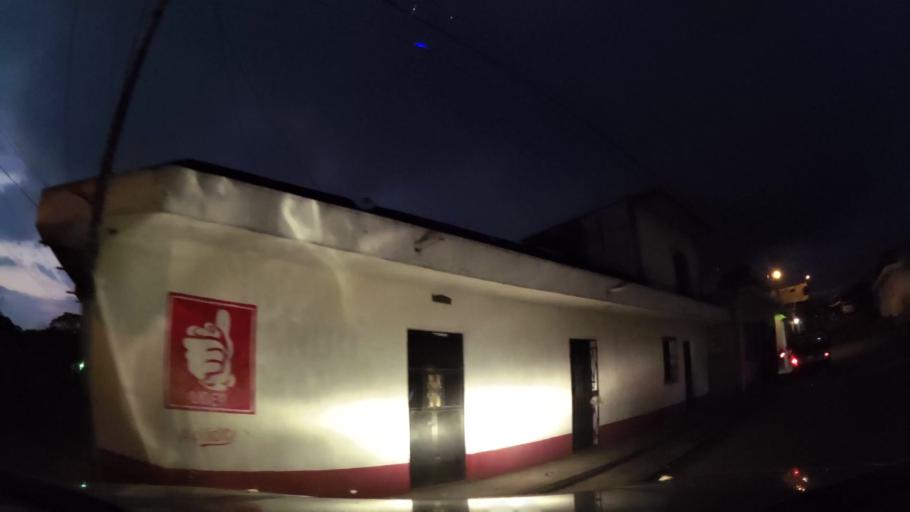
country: GT
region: Escuintla
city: Santa Lucia Cotzumalguapa
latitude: 14.3363
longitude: -91.0321
